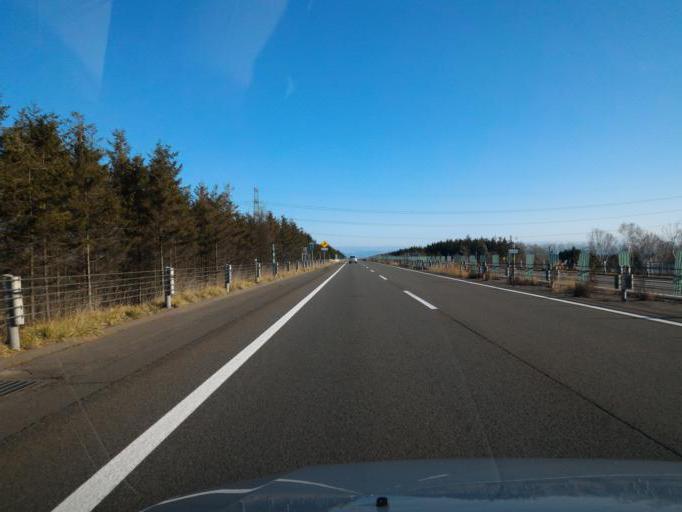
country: JP
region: Hokkaido
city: Ebetsu
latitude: 43.1185
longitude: 141.6260
